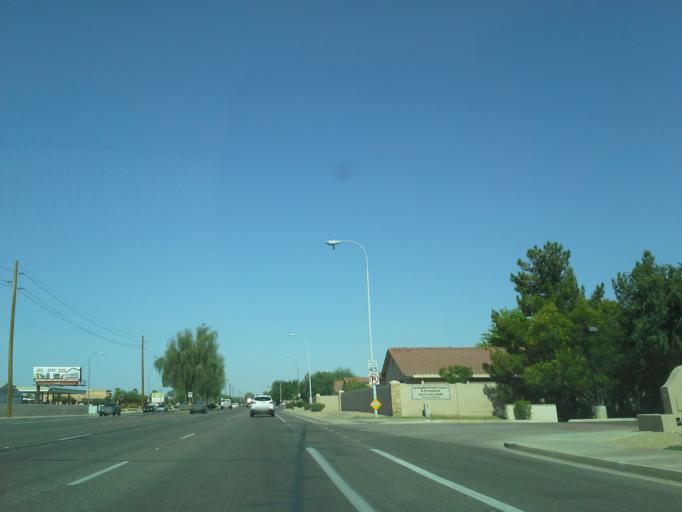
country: US
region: Arizona
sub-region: Maricopa County
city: Sun Lakes
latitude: 33.2187
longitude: -111.8223
